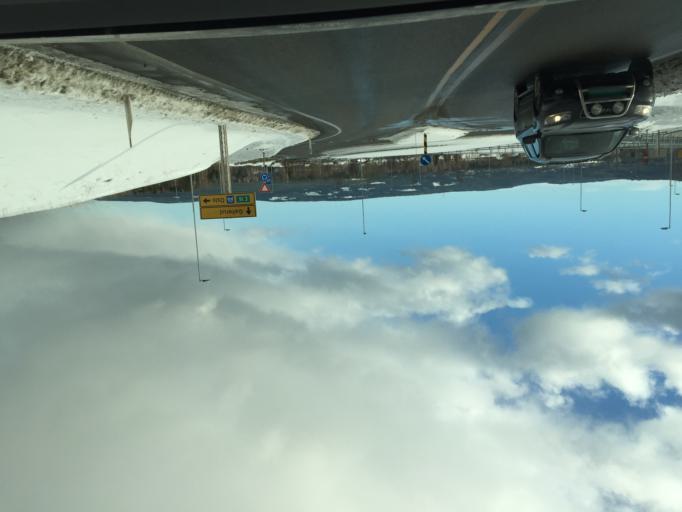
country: NO
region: Hedmark
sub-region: Kongsvinger
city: Spetalen
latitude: 60.2091
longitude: 11.8916
